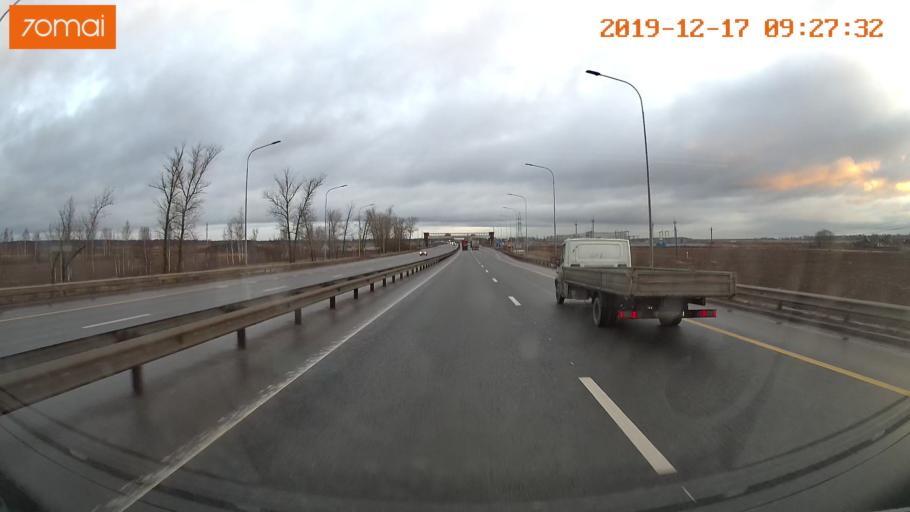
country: RU
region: Vladimir
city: Vorsha
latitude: 56.0519
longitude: 40.0899
